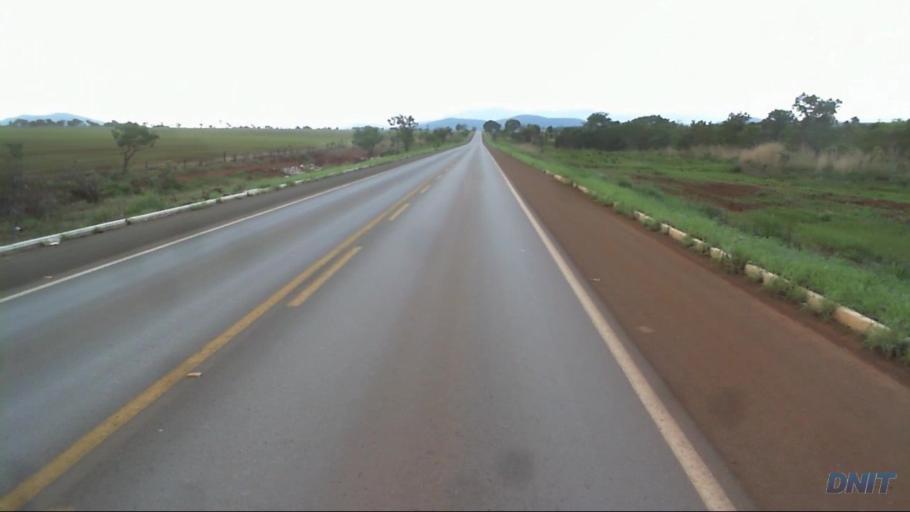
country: BR
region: Goias
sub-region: Barro Alto
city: Barro Alto
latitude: -14.8418
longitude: -49.0295
